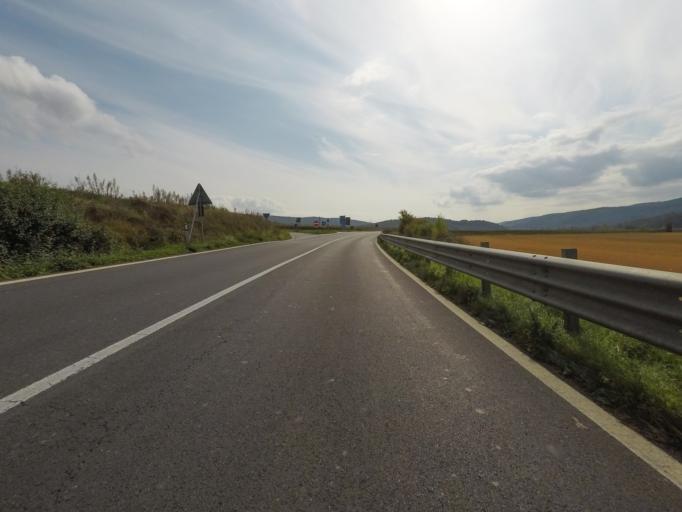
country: IT
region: Tuscany
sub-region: Provincia di Siena
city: Murlo
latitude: 43.1668
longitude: 11.2866
